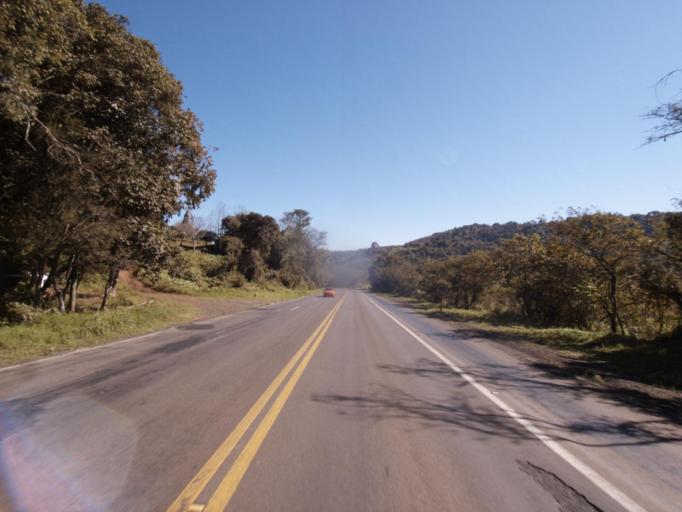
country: BR
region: Rio Grande do Sul
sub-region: Frederico Westphalen
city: Frederico Westphalen
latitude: -26.8191
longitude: -53.3704
